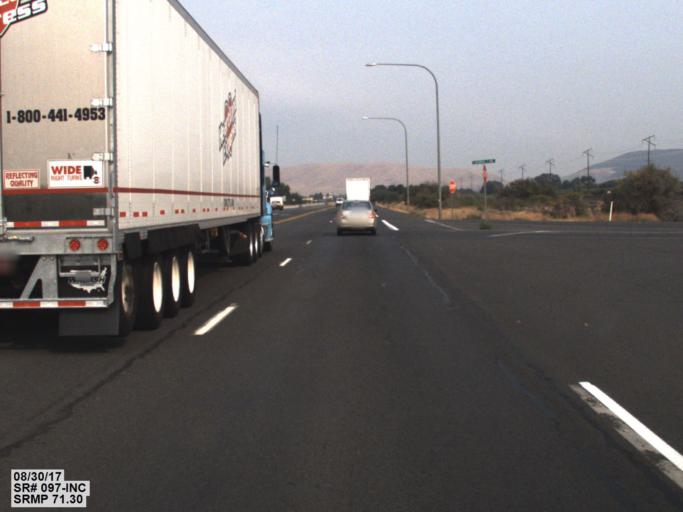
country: US
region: Washington
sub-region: Yakima County
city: Wapato
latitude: 46.4771
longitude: -120.4464
